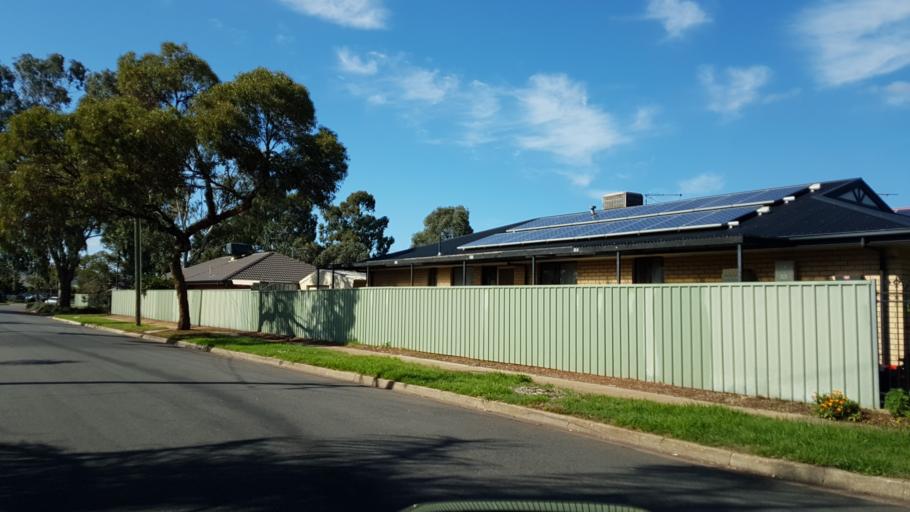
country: AU
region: South Australia
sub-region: Salisbury
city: Salisbury
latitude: -34.7529
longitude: 138.6387
